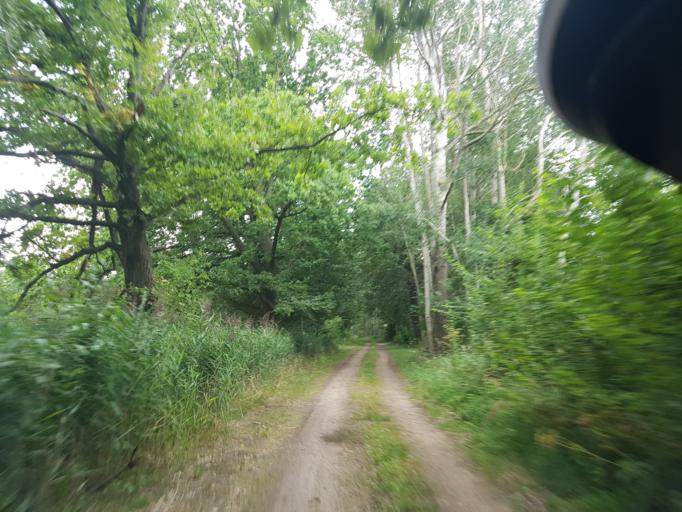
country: DE
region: Brandenburg
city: Ruckersdorf
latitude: 51.6001
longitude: 13.5697
